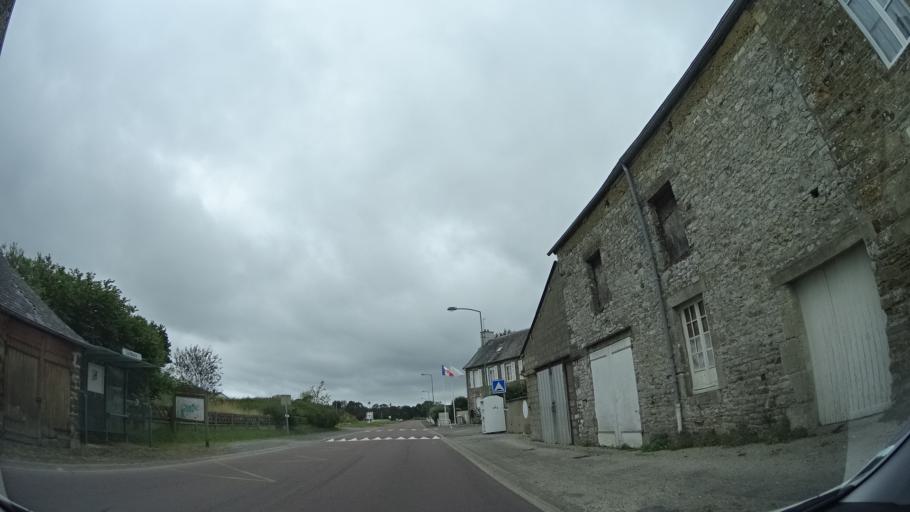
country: FR
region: Lower Normandy
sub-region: Departement de la Manche
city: La Haye-du-Puits
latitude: 49.3009
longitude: -1.5761
